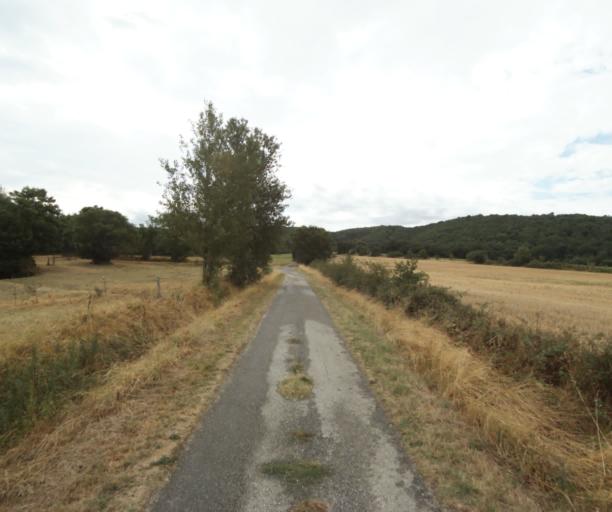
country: FR
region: Midi-Pyrenees
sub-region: Departement de la Haute-Garonne
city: Revel
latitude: 43.4176
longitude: 1.9791
